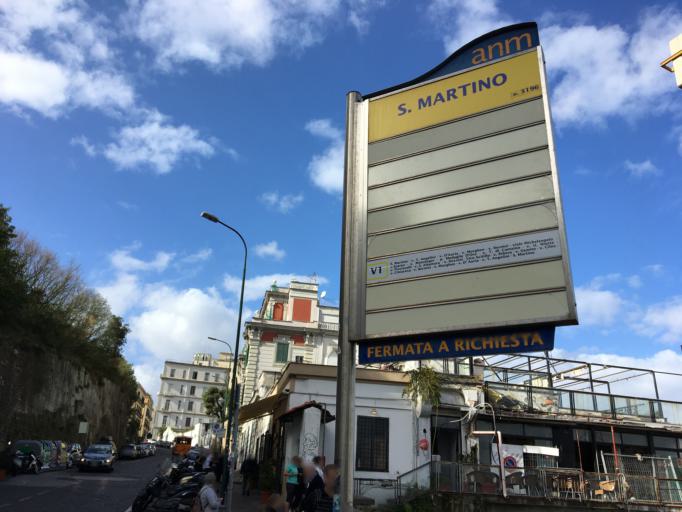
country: IT
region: Campania
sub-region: Provincia di Napoli
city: Napoli
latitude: 40.8444
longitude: 14.2402
